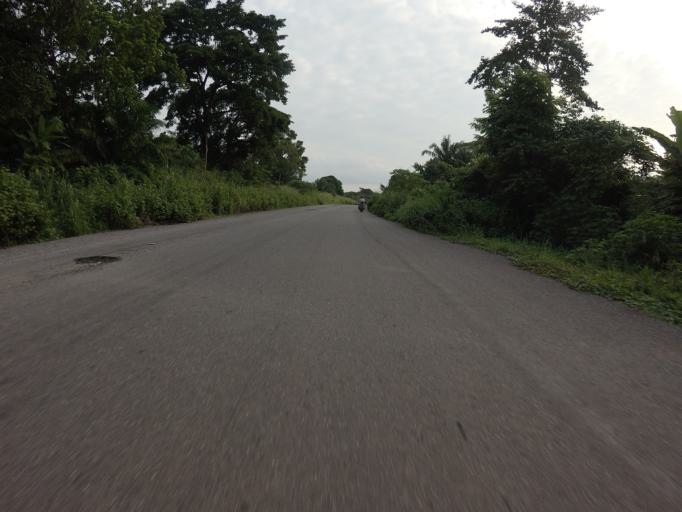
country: GH
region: Volta
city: Kpandu
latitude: 6.8695
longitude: 0.4160
